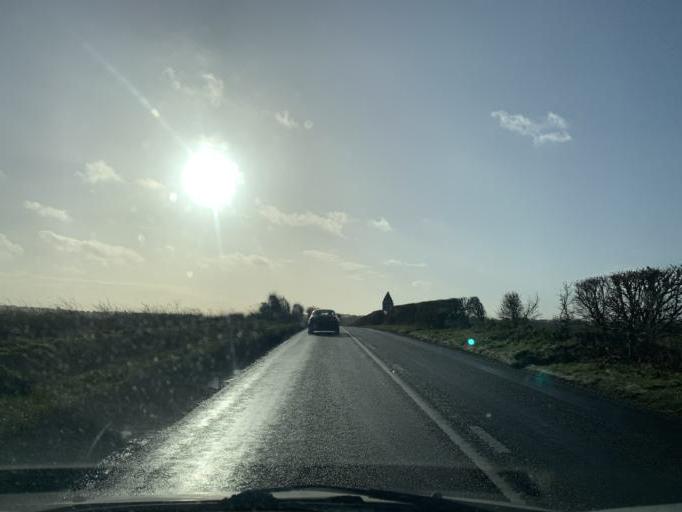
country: GB
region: England
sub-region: Wiltshire
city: Winterbourne Stoke
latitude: 51.1695
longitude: -1.8590
